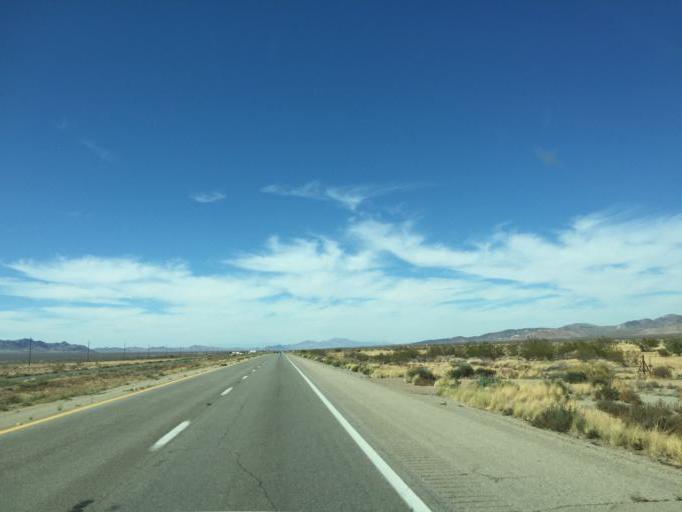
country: US
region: Arizona
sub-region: Mohave County
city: Dolan Springs
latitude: 35.5383
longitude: -114.3582
